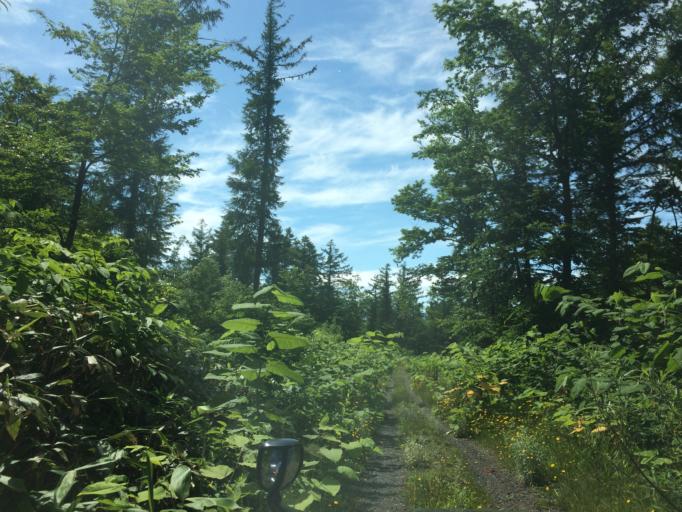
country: JP
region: Hokkaido
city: Niseko Town
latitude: 42.8653
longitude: 140.7968
